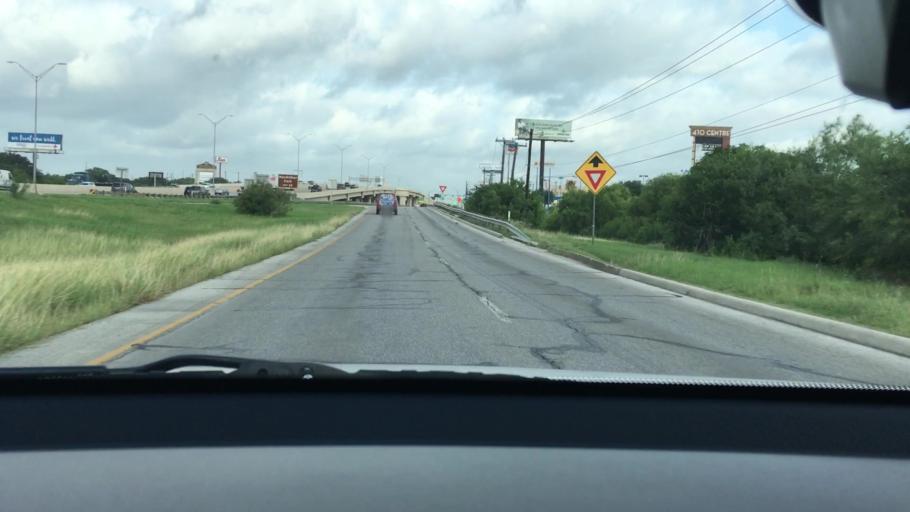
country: US
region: Texas
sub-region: Bexar County
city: Windcrest
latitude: 29.5165
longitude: -98.4067
